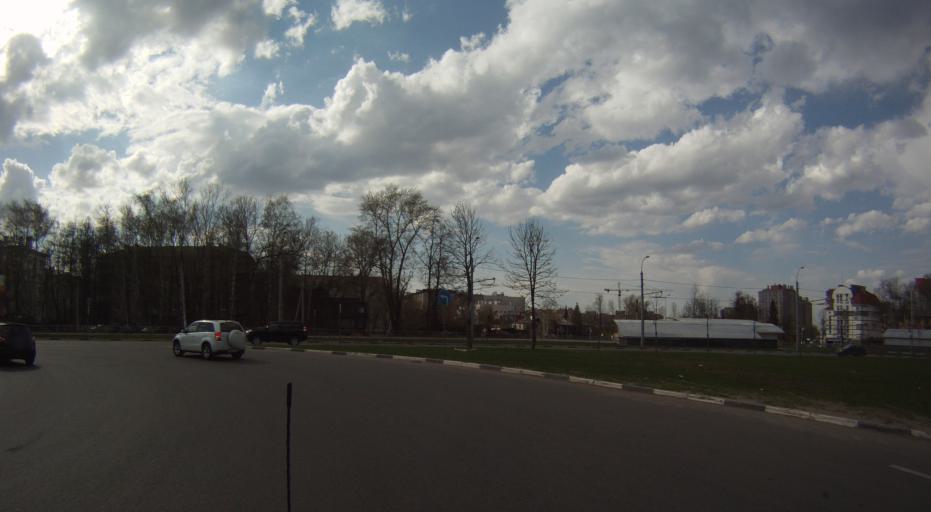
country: RU
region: Nizjnij Novgorod
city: Nizhniy Novgorod
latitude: 56.3093
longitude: 43.9853
